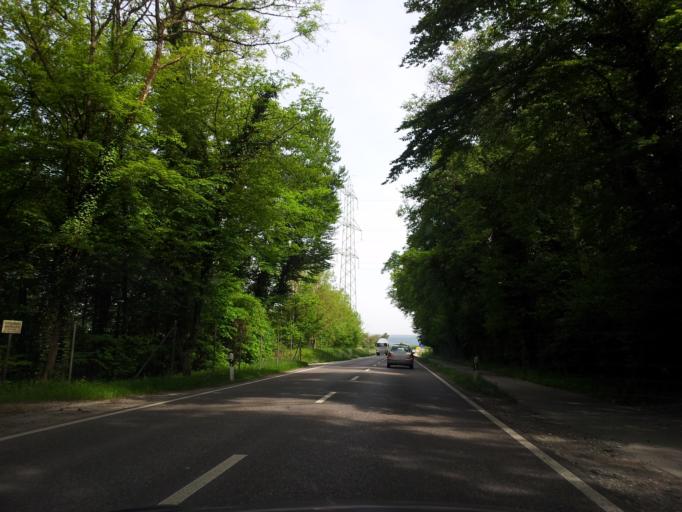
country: CH
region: Zurich
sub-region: Bezirk Buelach
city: Buelach / Soligaenter
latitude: 47.5481
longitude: 8.5300
